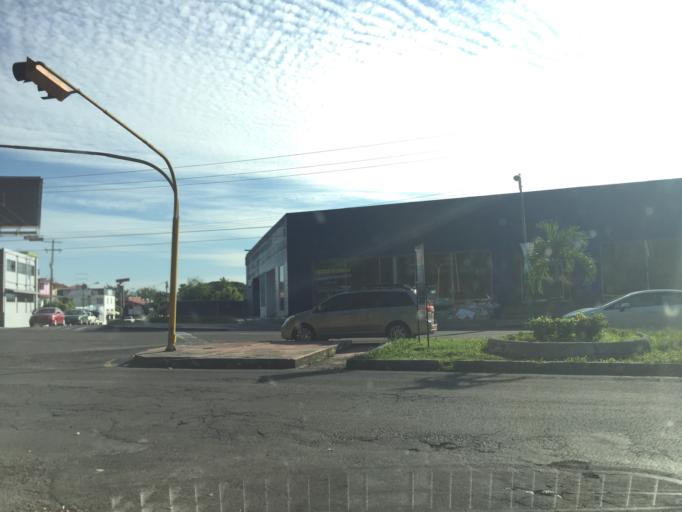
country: MX
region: Colima
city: Colima
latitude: 19.2582
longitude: -103.7192
